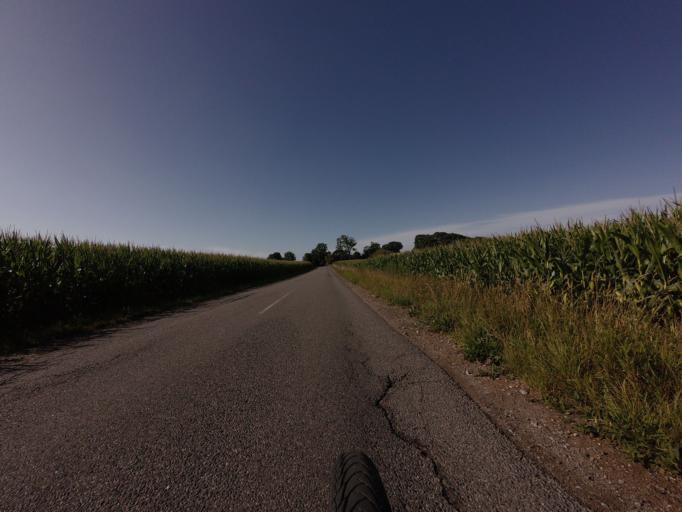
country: DK
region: North Denmark
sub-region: Hjorring Kommune
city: Vra
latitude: 57.3788
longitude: 10.0063
